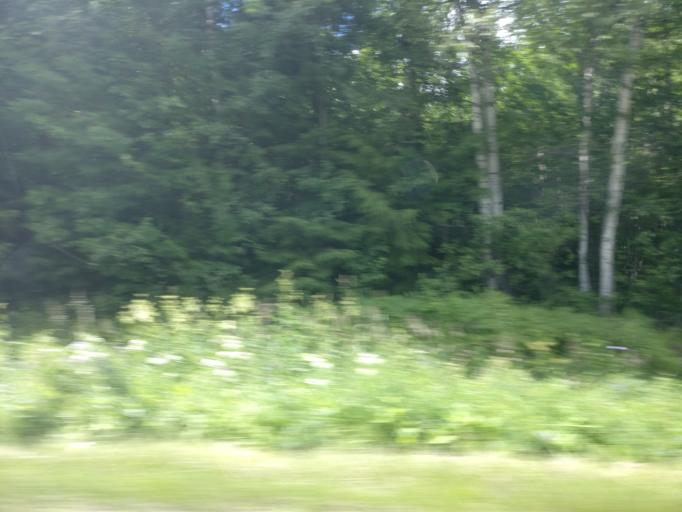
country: FI
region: Central Finland
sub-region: Joutsa
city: Joutsa
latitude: 61.7039
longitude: 26.0589
